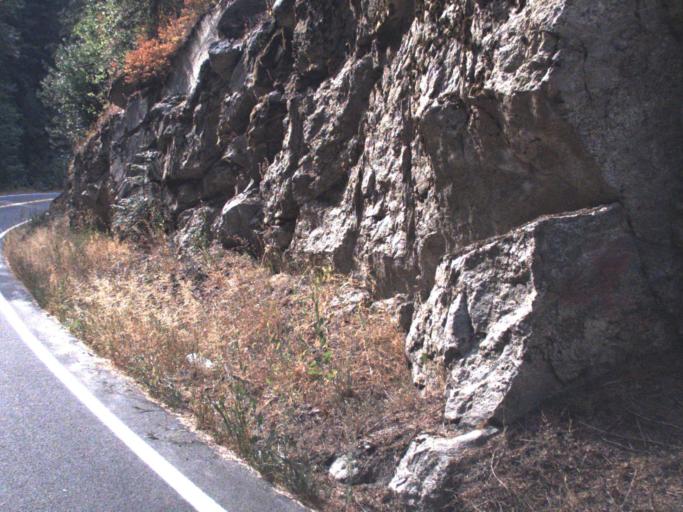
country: US
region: Washington
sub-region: Spokane County
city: Otis Orchards-East Farms
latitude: 47.8787
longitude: -117.1440
